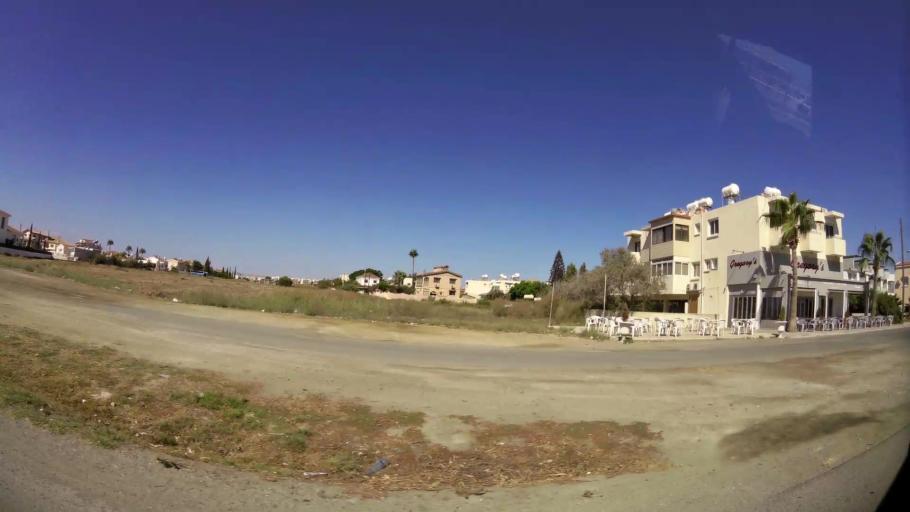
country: CY
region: Larnaka
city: Livadia
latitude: 34.9562
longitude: 33.6529
